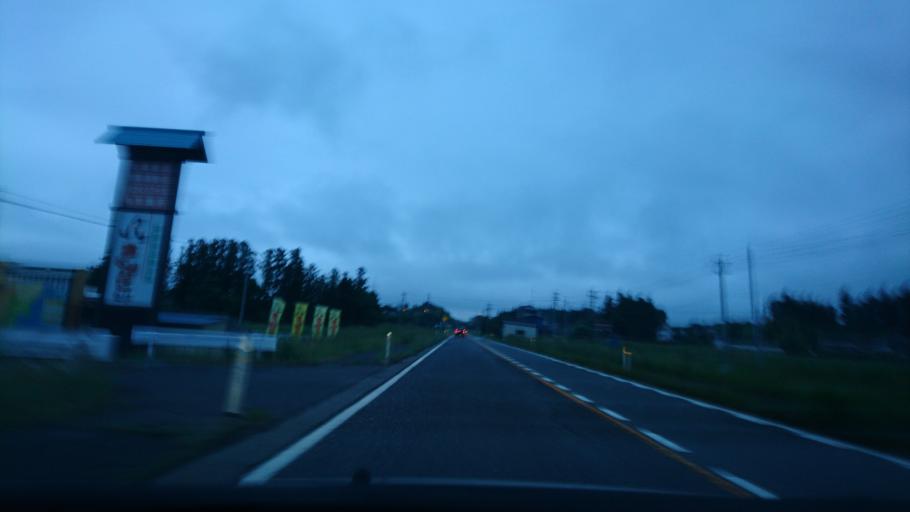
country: JP
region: Iwate
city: Ichinoseki
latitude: 38.8493
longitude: 141.0958
